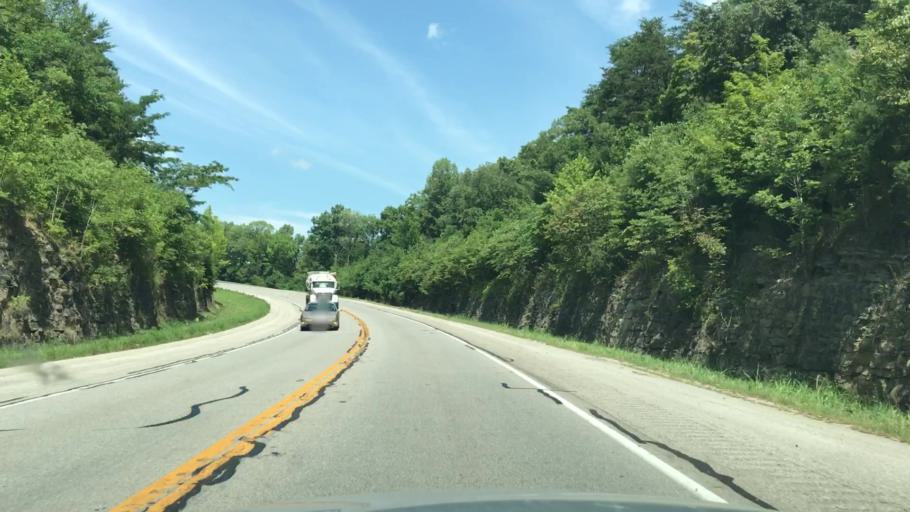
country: US
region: Kentucky
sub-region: Wayne County
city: Monticello
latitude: 36.8186
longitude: -84.8812
